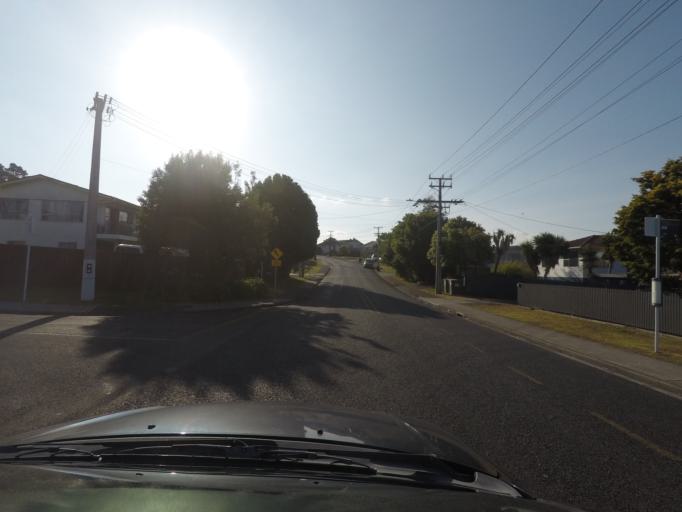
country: NZ
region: Auckland
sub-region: Auckland
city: Rosebank
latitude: -36.8575
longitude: 174.6485
